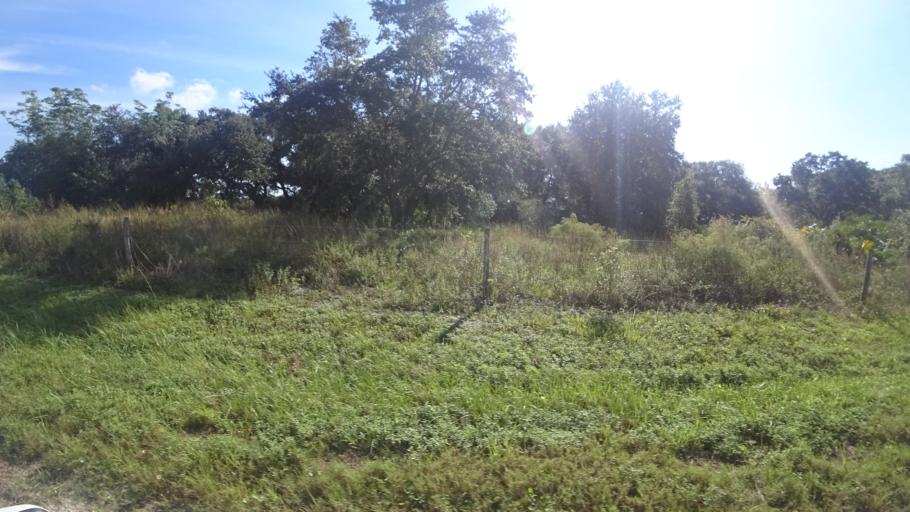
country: US
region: Florida
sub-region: Sarasota County
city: The Meadows
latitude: 27.4648
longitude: -82.3339
